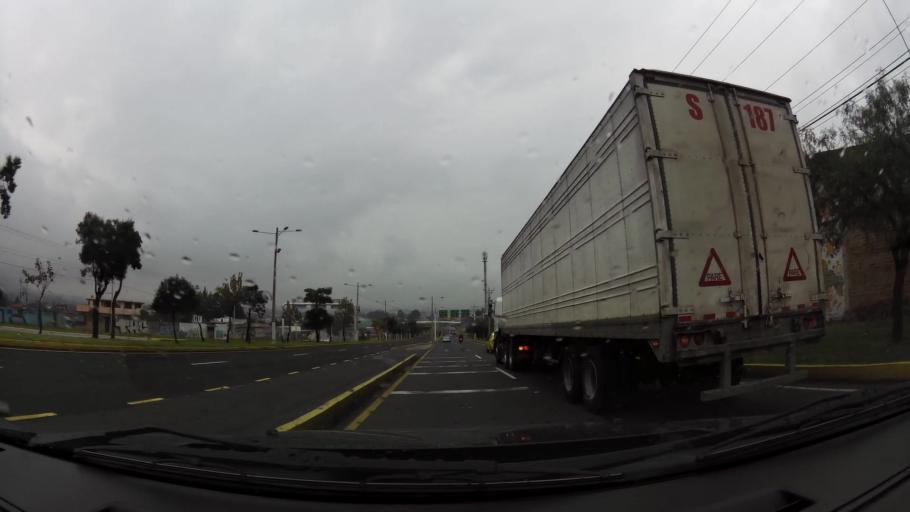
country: EC
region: Pichincha
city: Sangolqui
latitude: -0.2881
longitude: -78.4671
